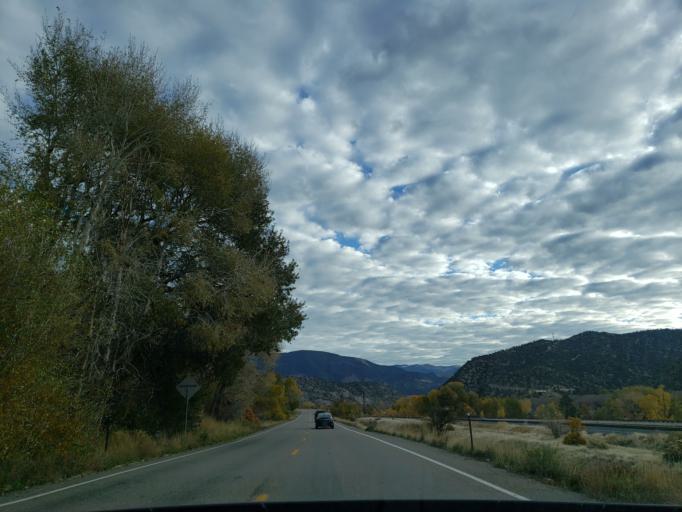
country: US
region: Colorado
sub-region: Garfield County
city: New Castle
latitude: 39.5599
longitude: -107.5574
